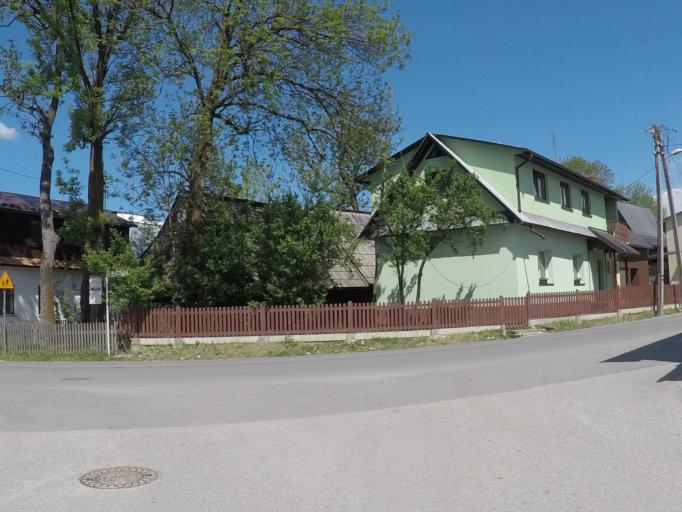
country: PL
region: Lesser Poland Voivodeship
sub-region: Powiat tatrzanski
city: Bukowina Tatrzanska
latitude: 49.3408
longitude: 20.1368
